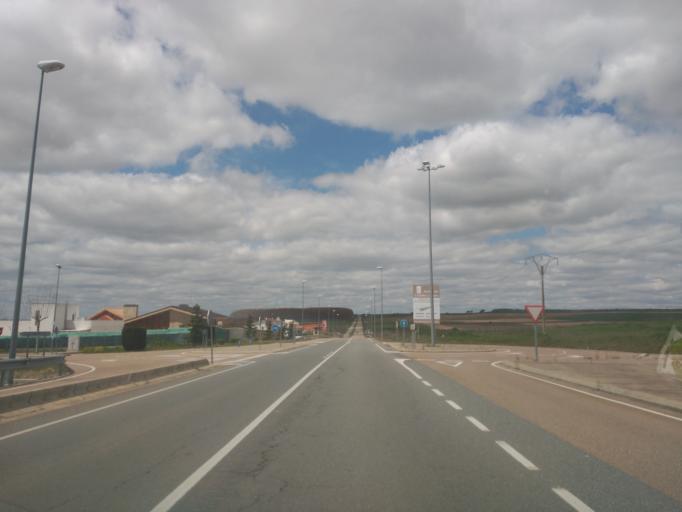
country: ES
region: Castille and Leon
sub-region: Provincia de Salamanca
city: Villamayor
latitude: 41.0166
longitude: -5.7149
